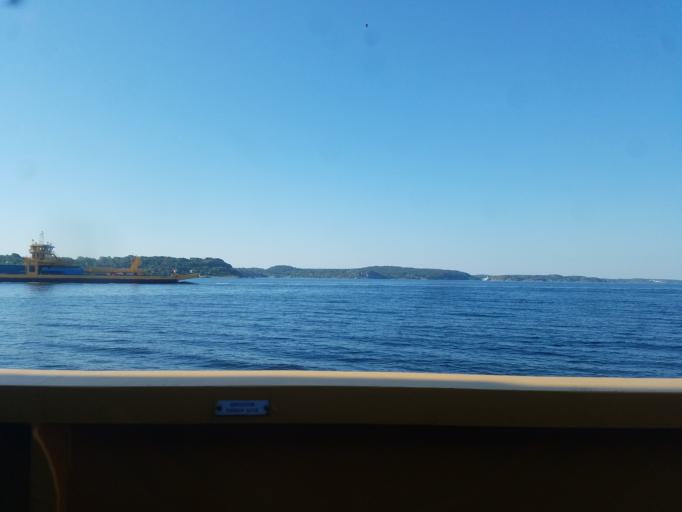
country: SE
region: Vaestra Goetaland
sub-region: Lysekils Kommun
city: Brastad
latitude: 58.3026
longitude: 11.5225
